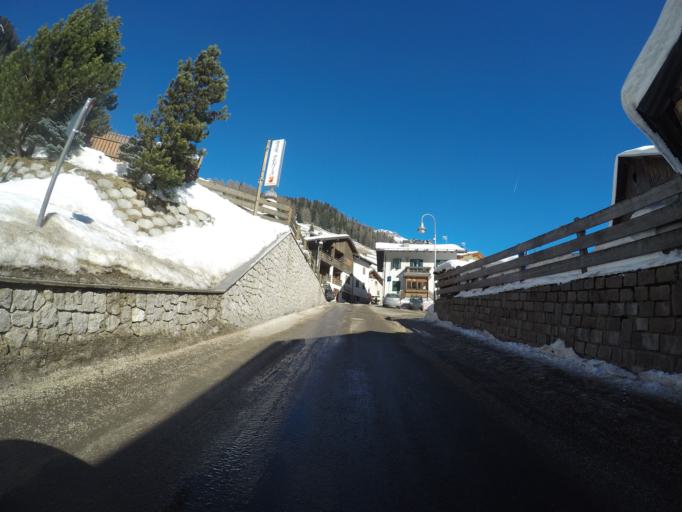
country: IT
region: Trentino-Alto Adige
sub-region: Provincia di Trento
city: Canazei
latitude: 46.4582
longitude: 11.7977
